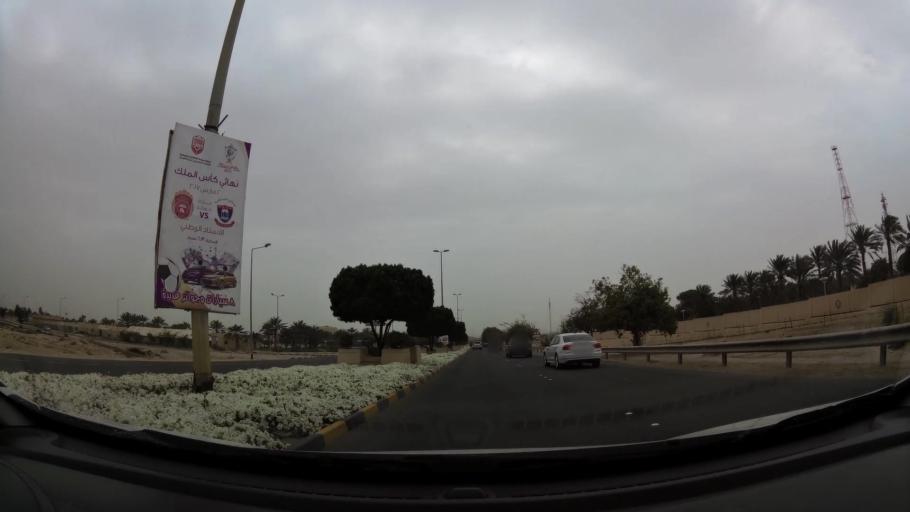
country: BH
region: Northern
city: Ar Rifa'
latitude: 26.1432
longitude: 50.5432
